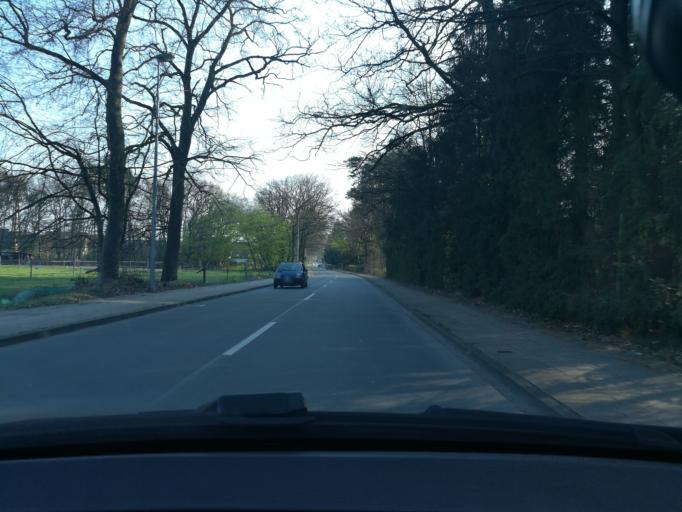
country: DE
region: North Rhine-Westphalia
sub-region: Regierungsbezirk Detmold
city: Bielefeld
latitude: 52.0030
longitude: 8.4753
